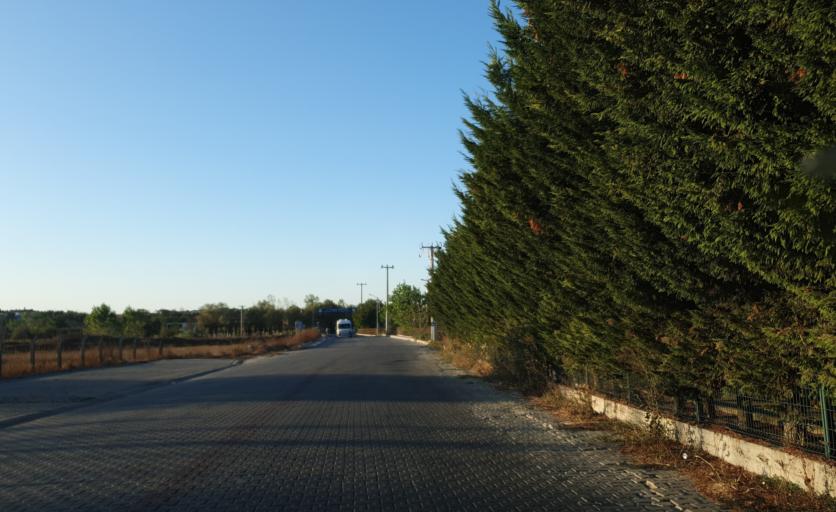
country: TR
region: Tekirdag
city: Beyazkoy
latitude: 41.3076
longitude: 27.7877
